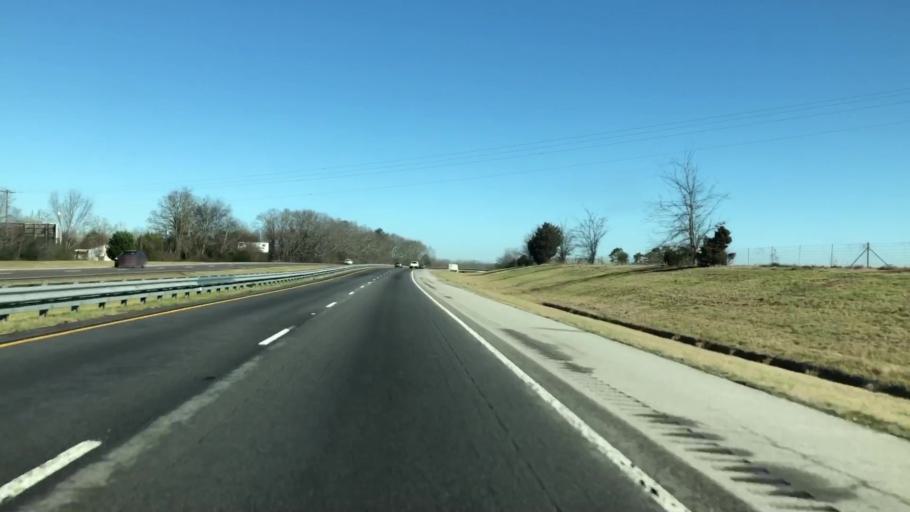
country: US
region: Alabama
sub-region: Limestone County
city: Athens
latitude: 34.8859
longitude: -86.9176
